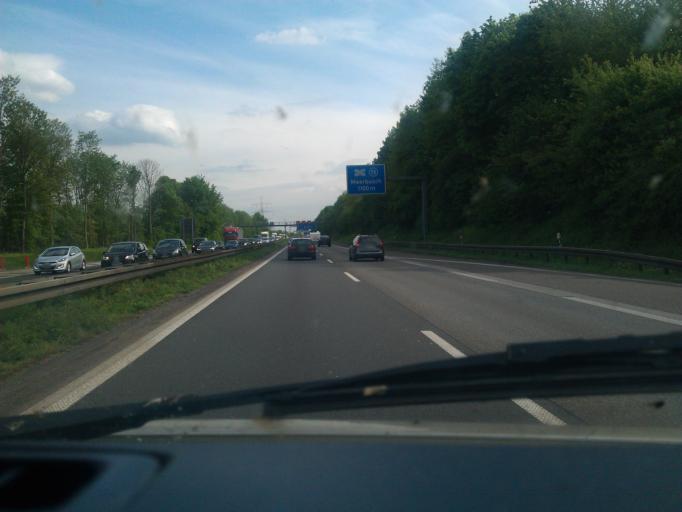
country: DE
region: North Rhine-Westphalia
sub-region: Regierungsbezirk Dusseldorf
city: Krefeld
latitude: 51.3096
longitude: 6.6341
